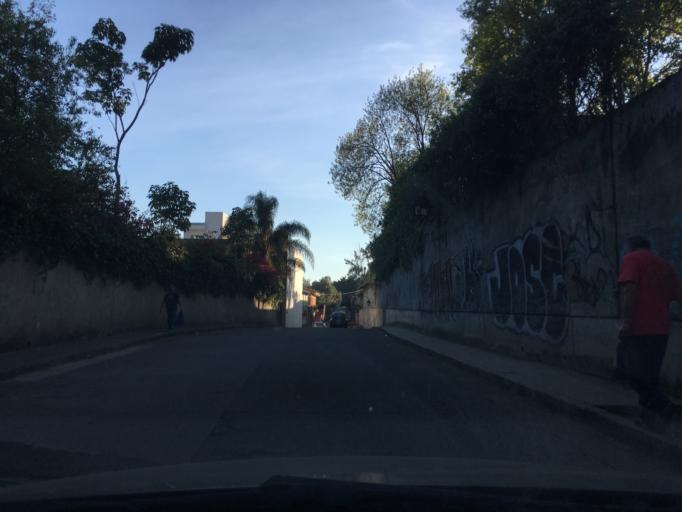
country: MX
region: Michoacan
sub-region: Uruapan
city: Uruapan
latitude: 19.4174
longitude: -102.0662
